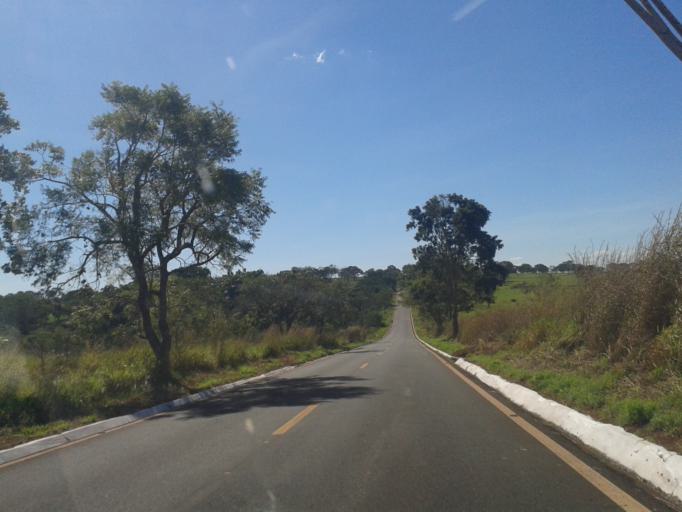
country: BR
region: Minas Gerais
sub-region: Ituiutaba
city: Ituiutaba
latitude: -19.1573
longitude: -49.7786
